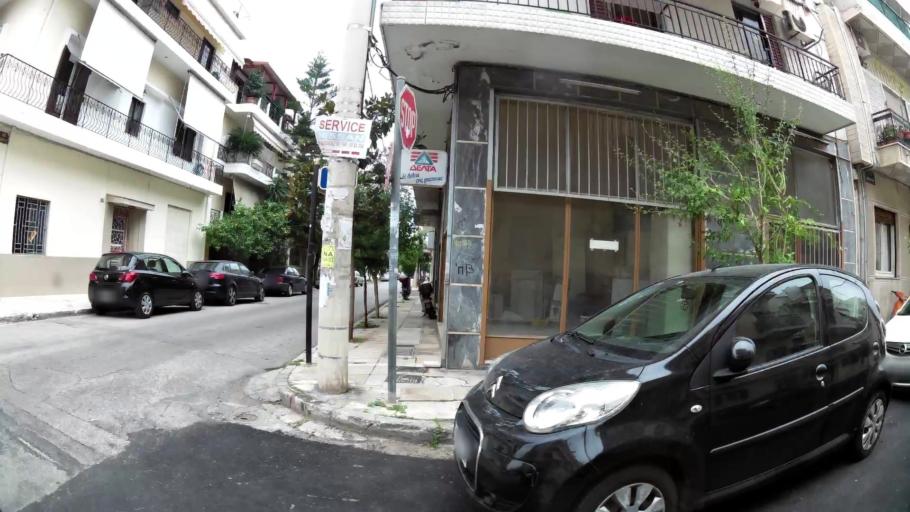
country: GR
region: Attica
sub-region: Nomarchia Athinas
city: Aigaleo
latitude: 37.9960
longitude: 23.6868
